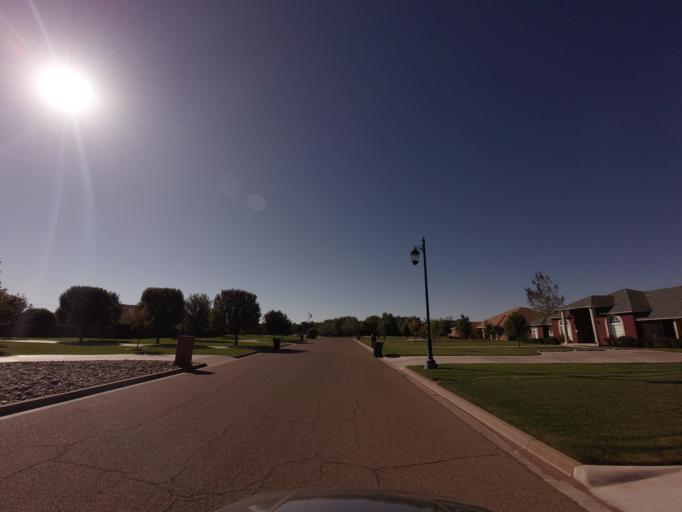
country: US
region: New Mexico
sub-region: Curry County
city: Clovis
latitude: 34.4322
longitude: -103.1675
